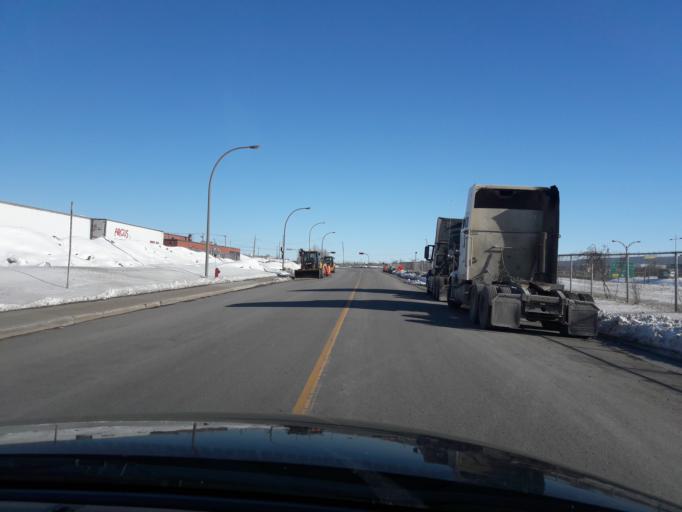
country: CA
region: Quebec
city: Dorval
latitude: 45.4834
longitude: -73.7248
